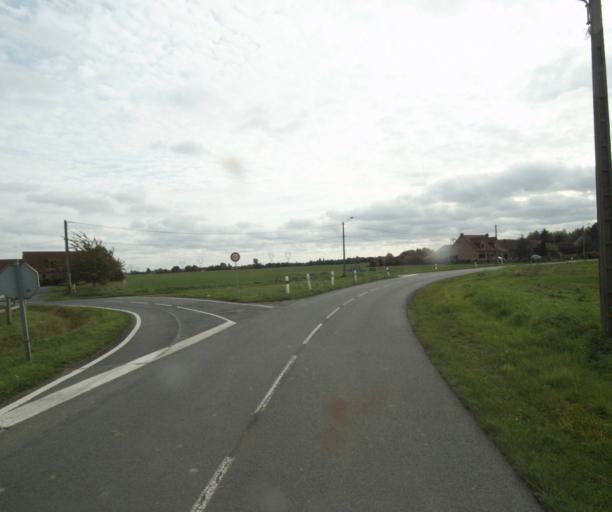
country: FR
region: Nord-Pas-de-Calais
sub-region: Departement du Nord
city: Bois-Grenier
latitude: 50.6611
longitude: 2.8751
